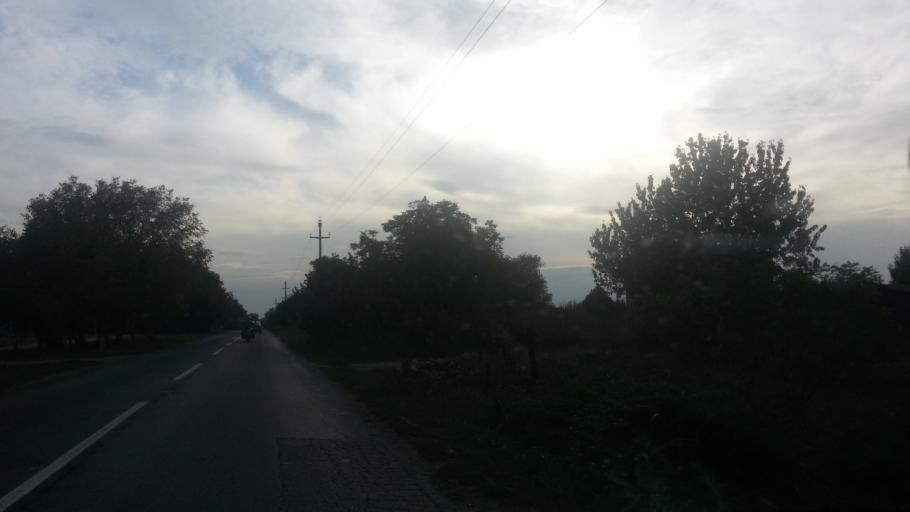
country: RS
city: Stari Banovci
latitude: 44.9994
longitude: 20.3000
